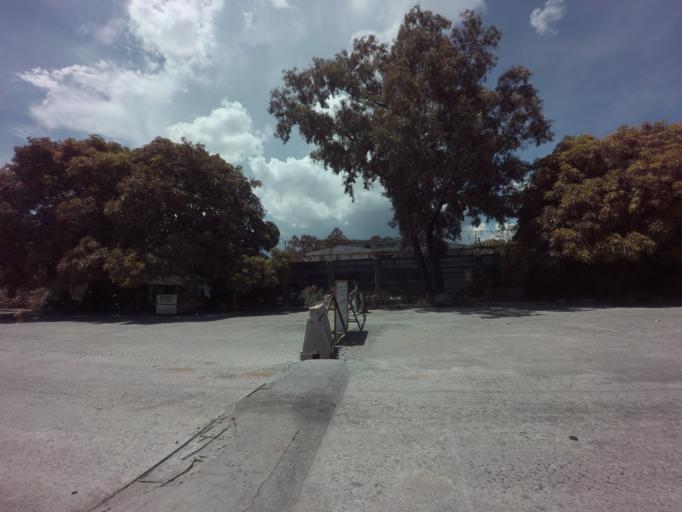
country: PH
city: Sambayanihan People's Village
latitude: 14.5065
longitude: 120.9865
